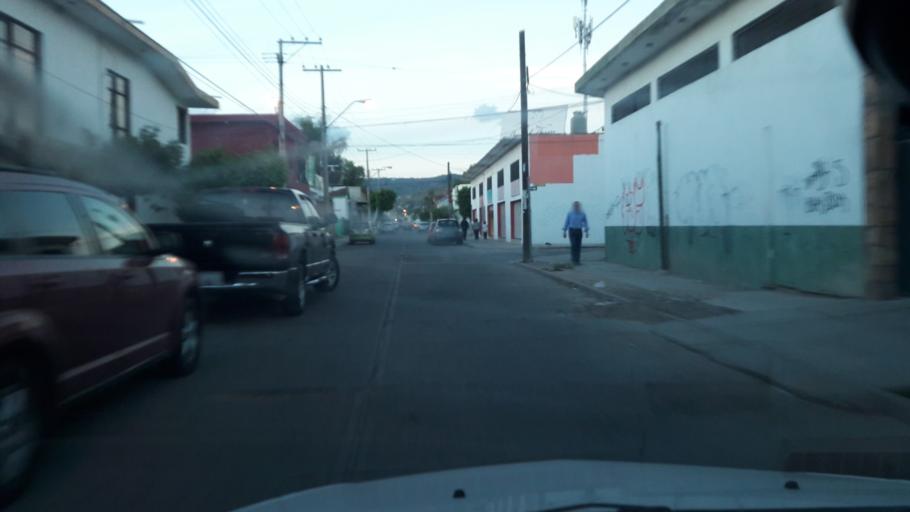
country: MX
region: Guanajuato
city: Leon
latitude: 21.1774
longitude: -101.6654
